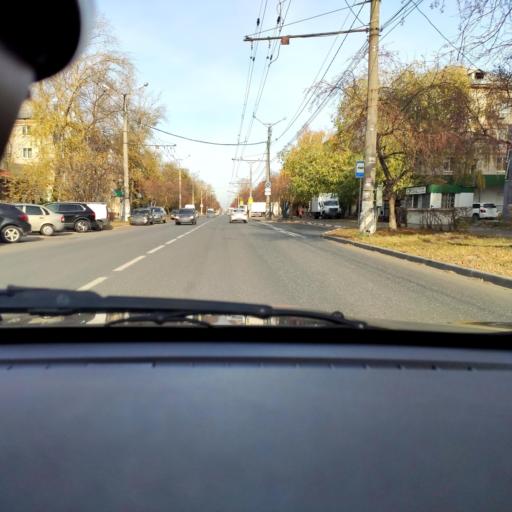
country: RU
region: Samara
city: Tol'yatti
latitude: 53.5121
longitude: 49.4181
